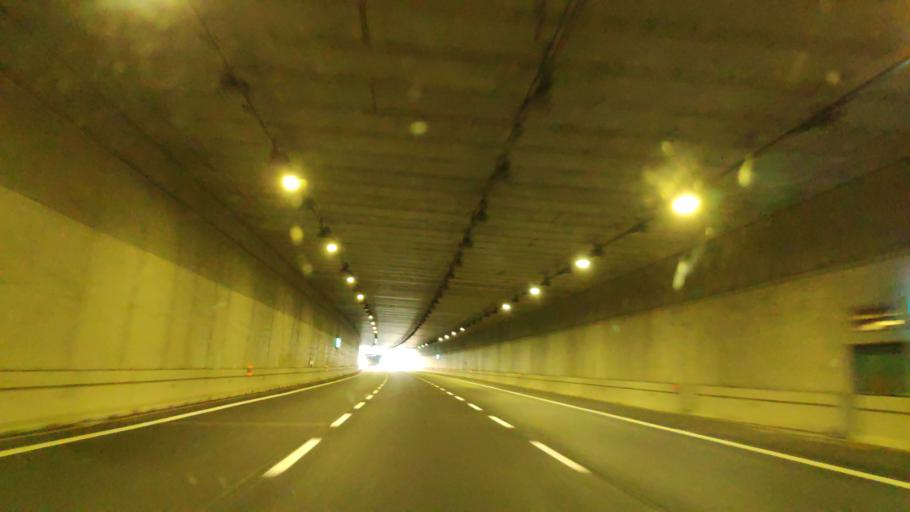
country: IT
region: Lombardy
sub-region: Citta metropolitana di Milano
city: Gessate
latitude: 45.5409
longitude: 9.4334
